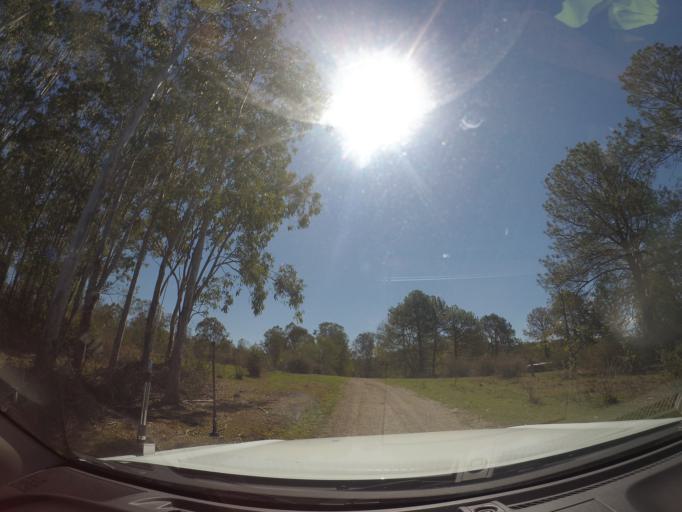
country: AU
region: Queensland
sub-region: Ipswich
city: Springfield Lakes
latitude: -27.7543
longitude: 152.8797
